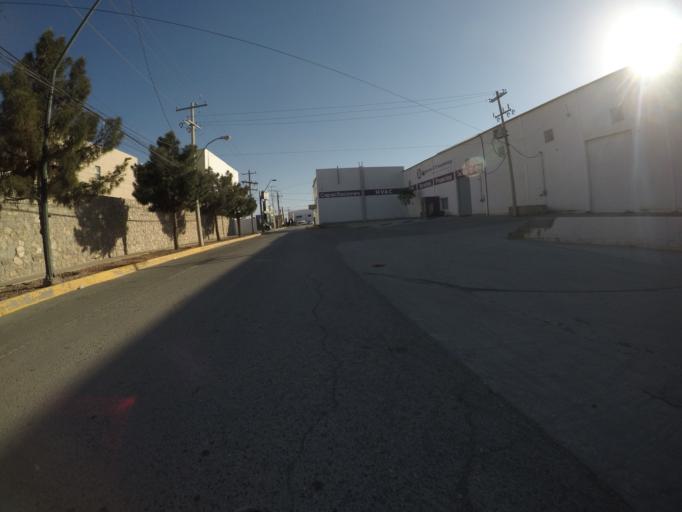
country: MX
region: Chihuahua
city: Ciudad Juarez
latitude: 31.7025
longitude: -106.3984
